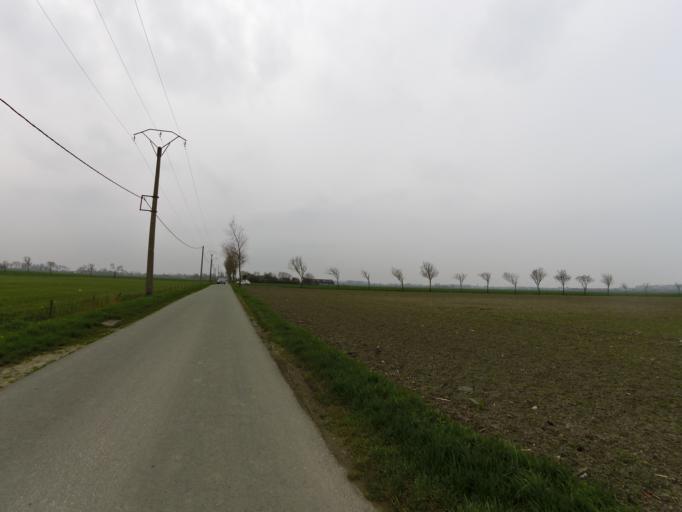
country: BE
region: Flanders
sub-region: Provincie West-Vlaanderen
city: Middelkerke
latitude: 51.1651
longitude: 2.8097
